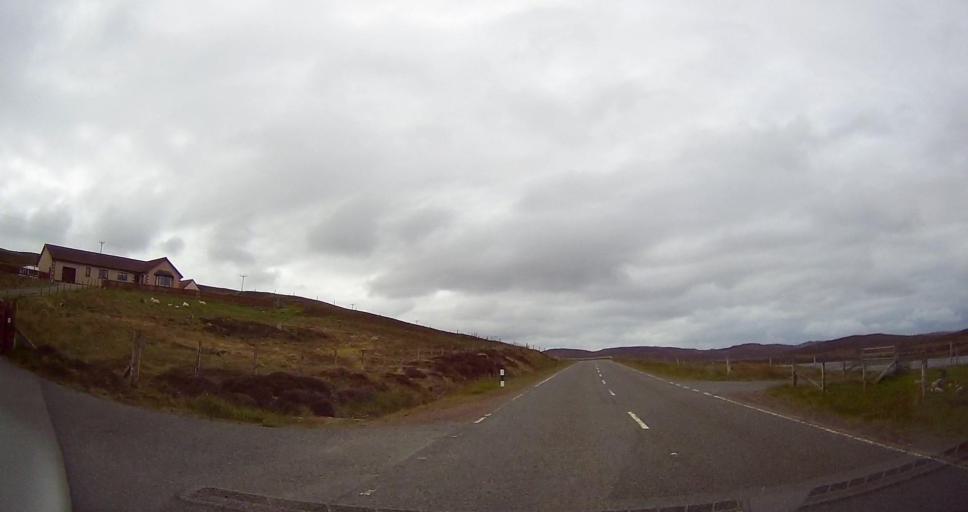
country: GB
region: Scotland
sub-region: Shetland Islands
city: Lerwick
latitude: 60.2555
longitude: -1.4642
